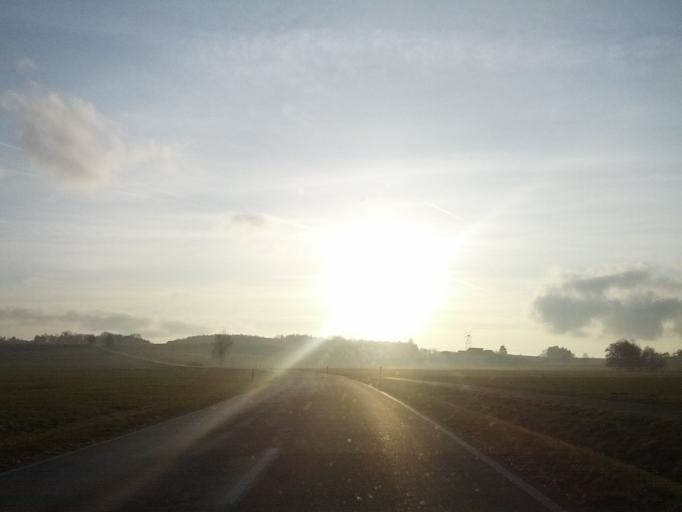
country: DE
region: Baden-Wuerttemberg
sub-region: Tuebingen Region
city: Steinhausen an der Rottum
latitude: 48.0420
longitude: 9.9615
